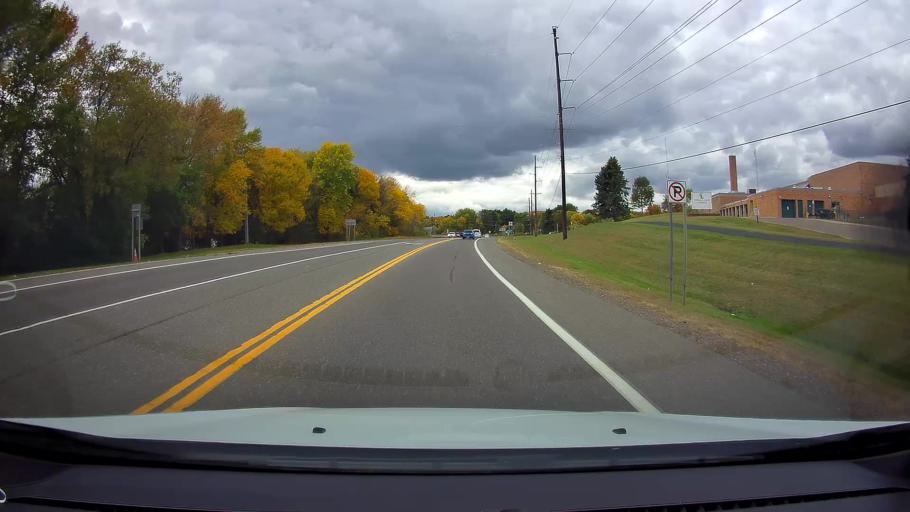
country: US
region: Minnesota
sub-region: Chisago County
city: Center City
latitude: 45.3898
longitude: -92.8269
